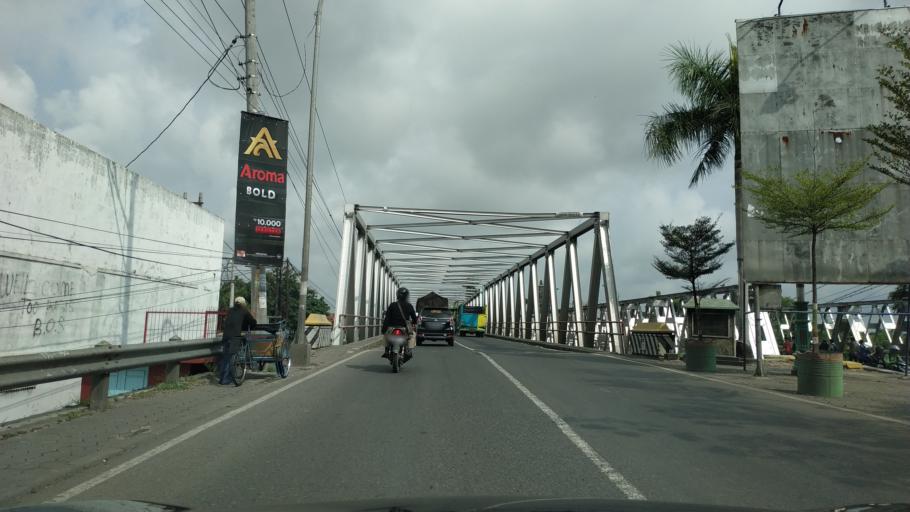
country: ID
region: Central Java
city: Dukuhturi
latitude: -6.8696
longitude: 109.0349
